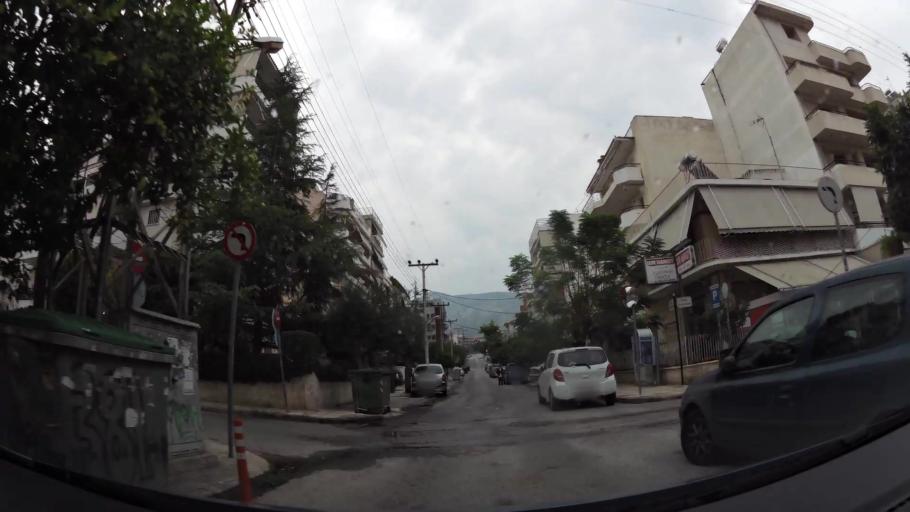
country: GR
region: Attica
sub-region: Nomarchia Athinas
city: Agios Dimitrios
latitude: 37.9201
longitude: 23.7423
